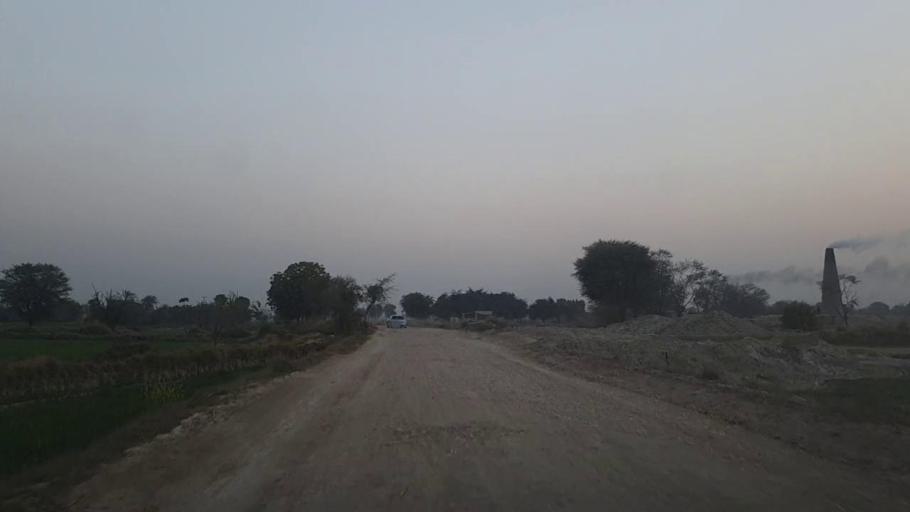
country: PK
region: Sindh
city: Naushahro Firoz
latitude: 26.8575
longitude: 68.0488
